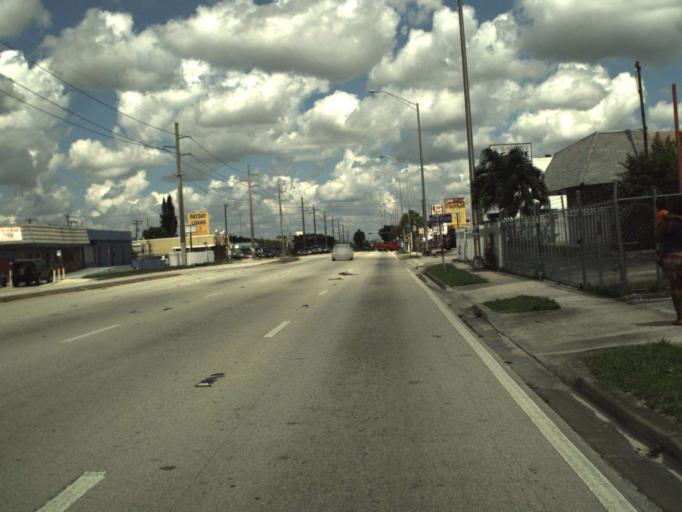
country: US
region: Florida
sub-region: Miami-Dade County
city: Golden Glades
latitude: 25.9068
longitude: -80.2115
